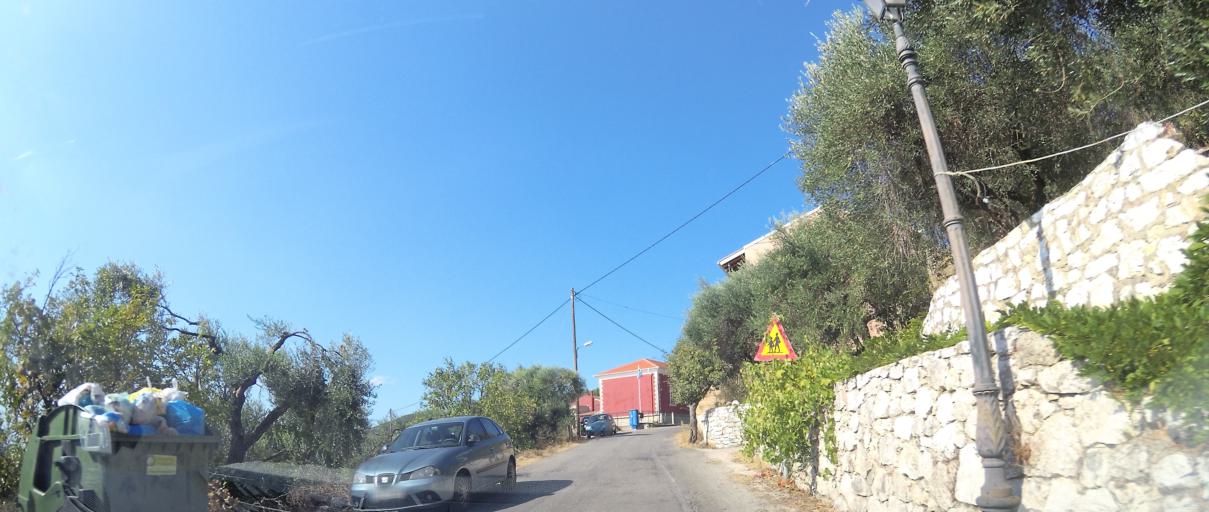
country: GR
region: Ionian Islands
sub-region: Nomos Kerkyras
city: Kontokali
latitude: 39.7205
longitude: 19.8450
